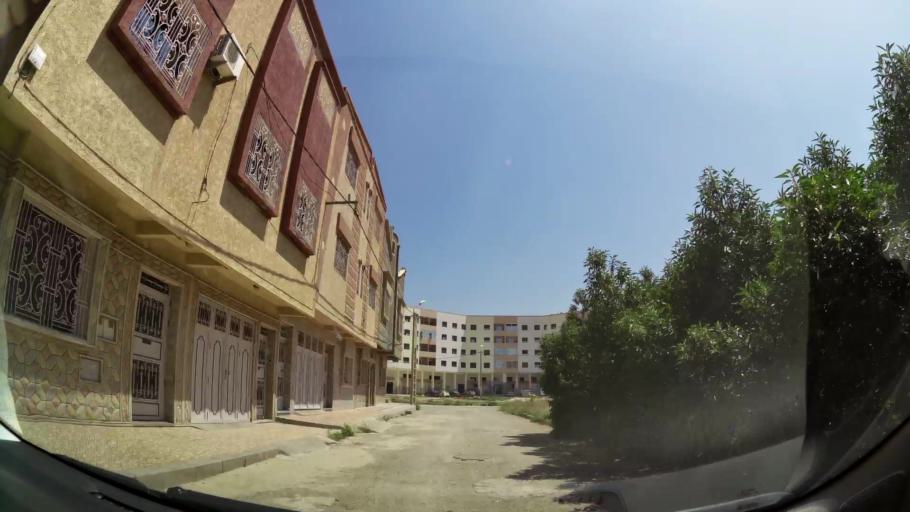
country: MA
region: Oriental
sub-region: Oujda-Angad
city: Oujda
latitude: 34.7001
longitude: -1.8896
